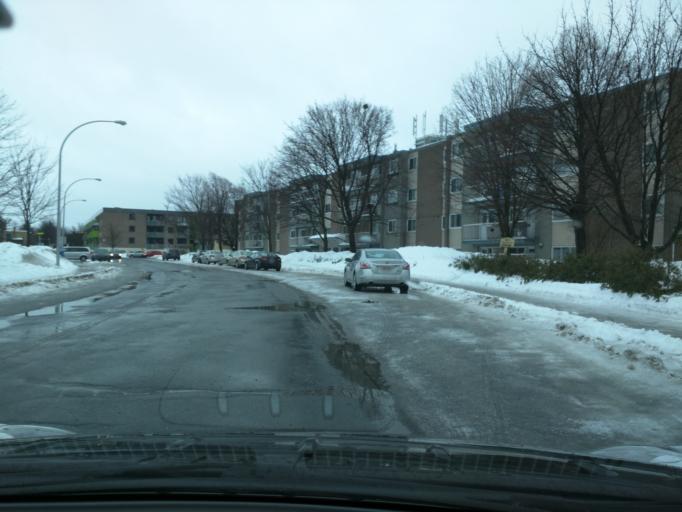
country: CA
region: Quebec
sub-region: Monteregie
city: Longueuil
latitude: 45.5237
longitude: -73.4579
